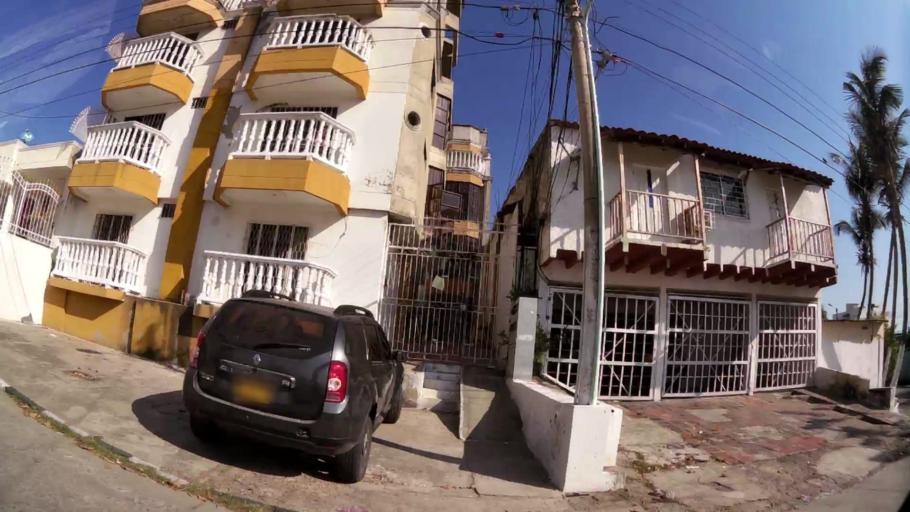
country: CO
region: Bolivar
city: Cartagena
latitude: 10.3890
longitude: -75.5169
